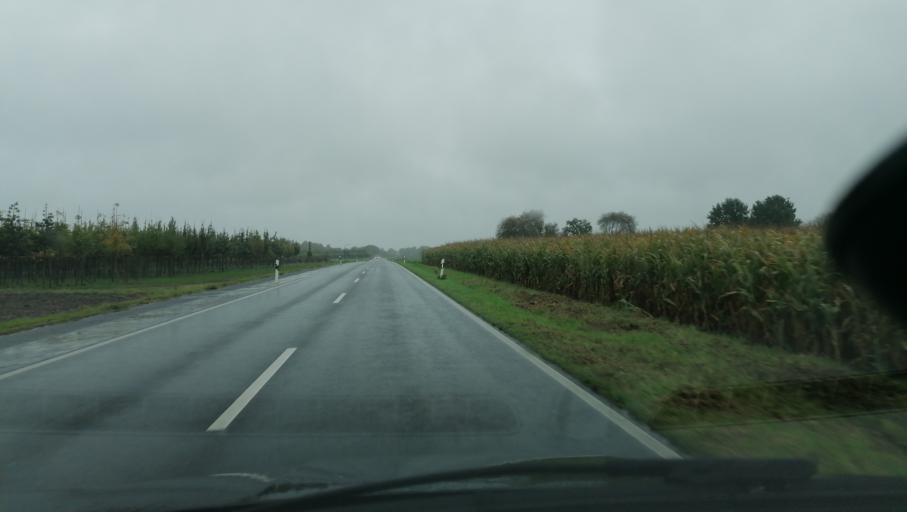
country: DE
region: North Rhine-Westphalia
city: Oer-Erkenschwick
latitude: 51.6224
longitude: 7.2879
